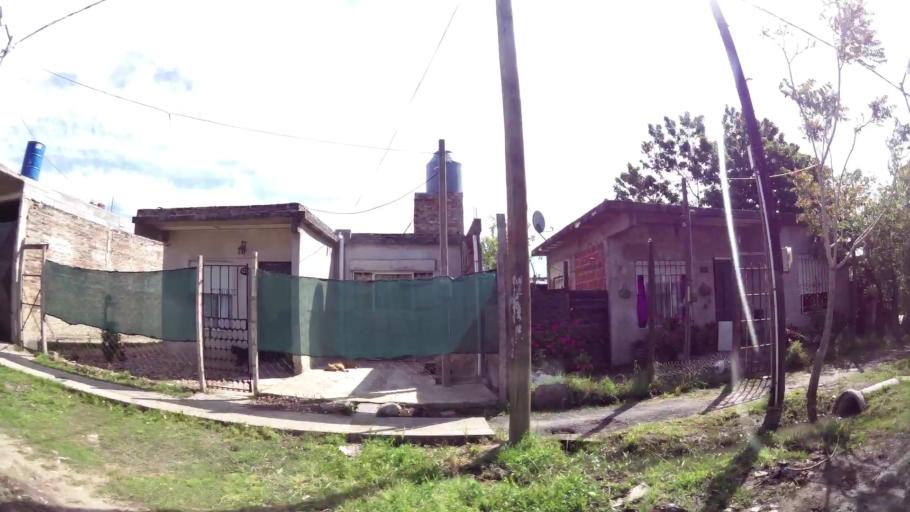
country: AR
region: Buenos Aires
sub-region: Partido de Quilmes
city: Quilmes
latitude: -34.7807
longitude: -58.2972
